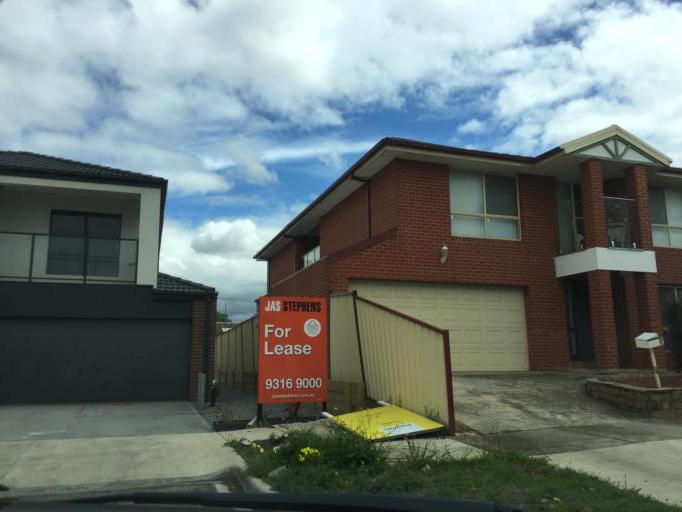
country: AU
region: Victoria
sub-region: Maribyrnong
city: Braybrook
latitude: -37.7938
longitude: 144.8553
